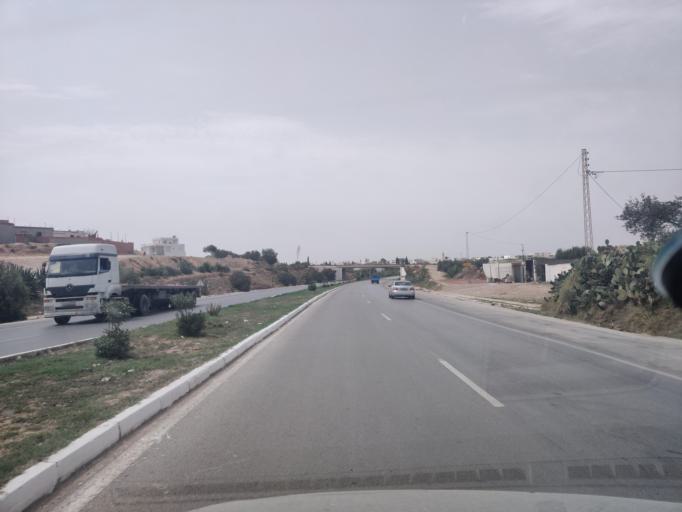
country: TN
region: Susah
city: Akouda
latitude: 35.8337
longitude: 10.5699
